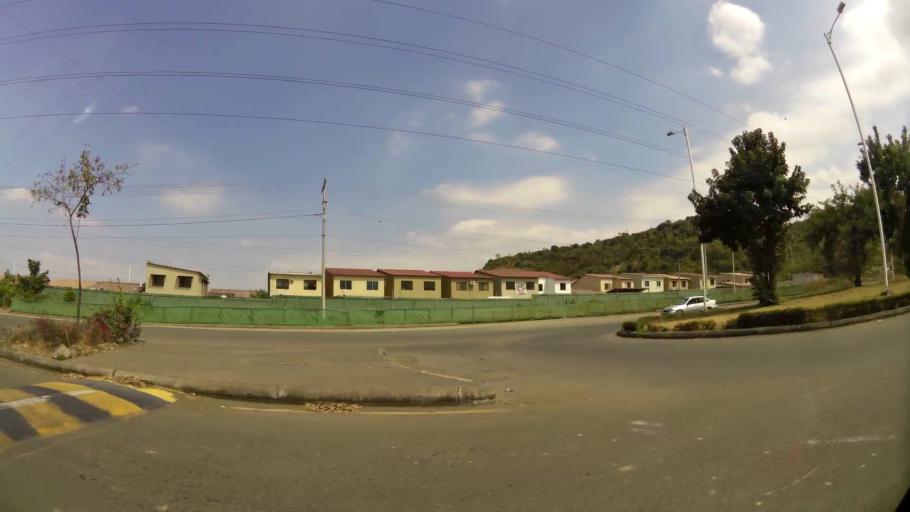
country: EC
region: Guayas
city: El Triunfo
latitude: -2.0340
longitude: -79.8997
